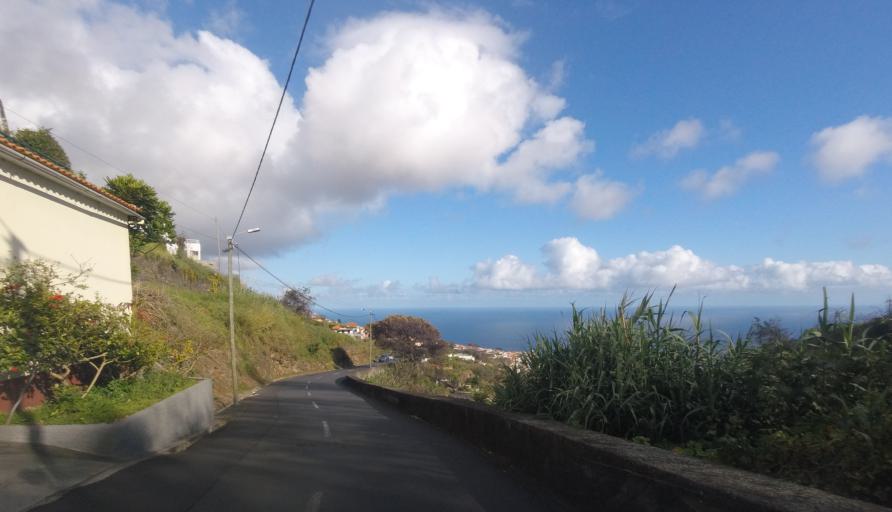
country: PT
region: Madeira
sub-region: Funchal
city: Nossa Senhora do Monte
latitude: 32.6676
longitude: -16.9024
